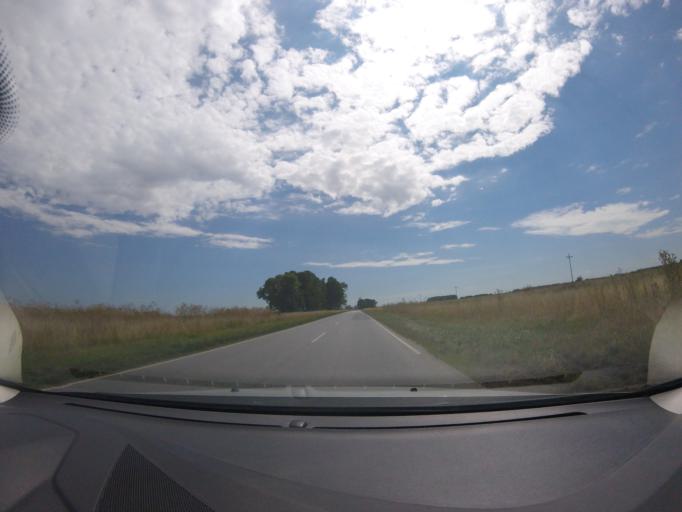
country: AR
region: Buenos Aires
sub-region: Partido de Tandil
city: Tandil
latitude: -37.2404
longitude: -59.1125
